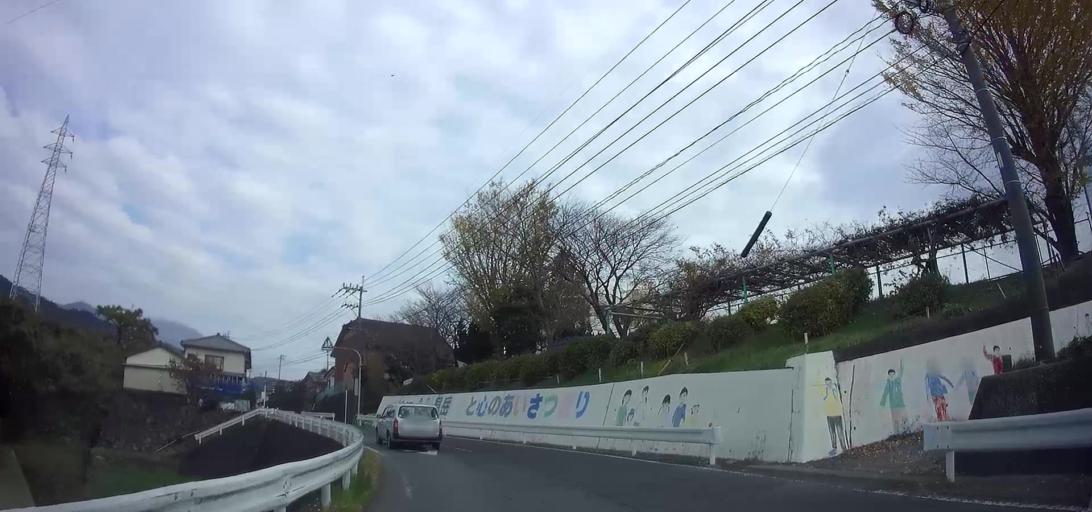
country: JP
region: Nagasaki
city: Shimabara
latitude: 32.6883
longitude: 130.2951
